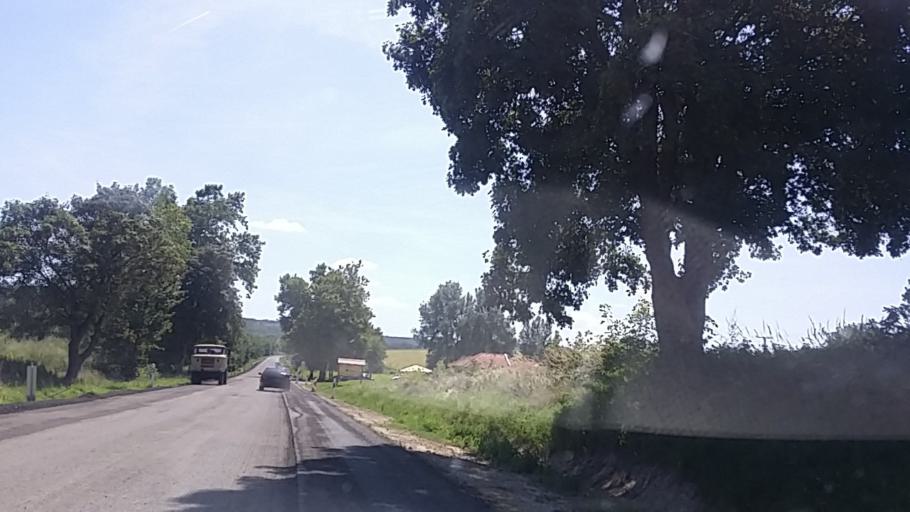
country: HU
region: Somogy
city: Adand
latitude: 46.7904
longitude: 18.1468
